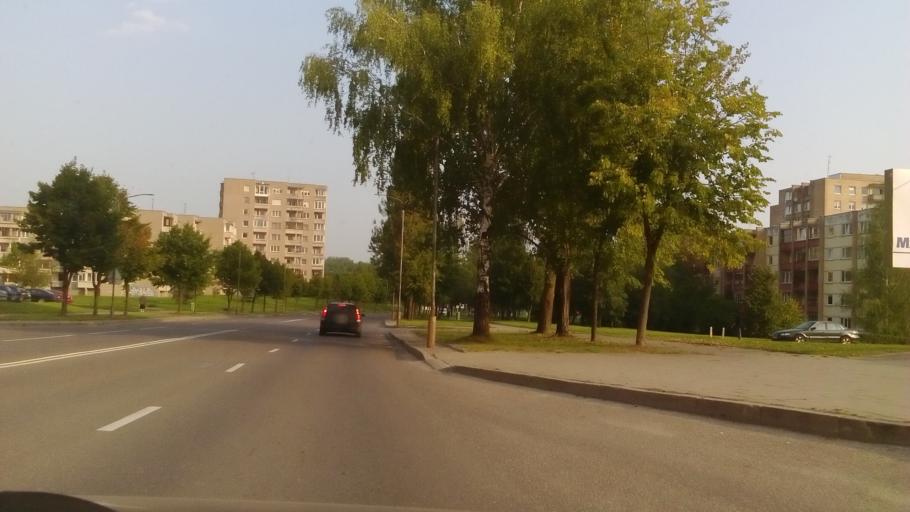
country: LT
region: Alytaus apskritis
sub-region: Alytus
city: Alytus
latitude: 54.3970
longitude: 24.0161
